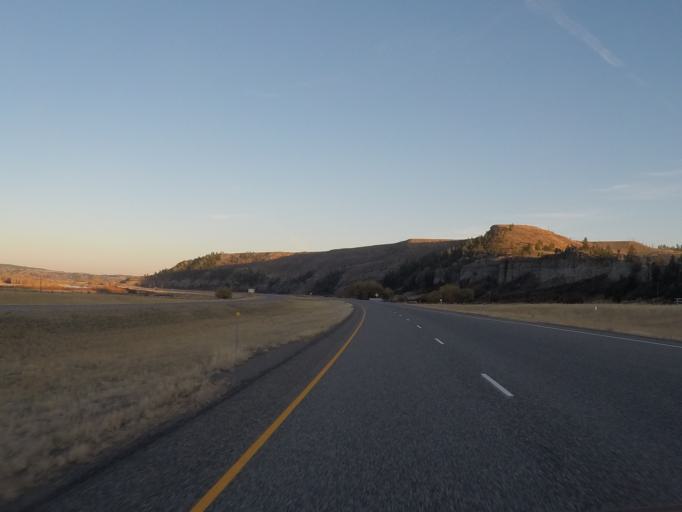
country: US
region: Montana
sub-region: Sweet Grass County
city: Big Timber
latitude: 45.7333
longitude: -109.7530
